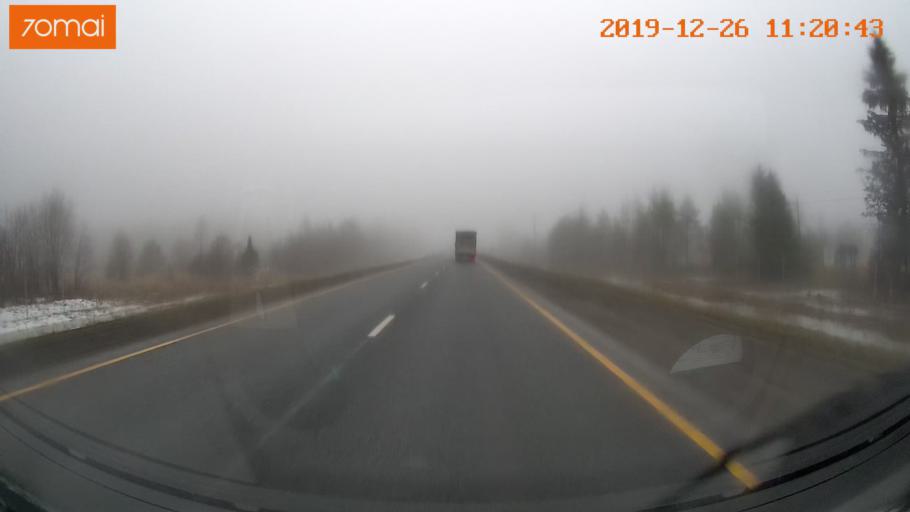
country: RU
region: Vologda
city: Chebsara
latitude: 59.1204
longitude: 38.9826
